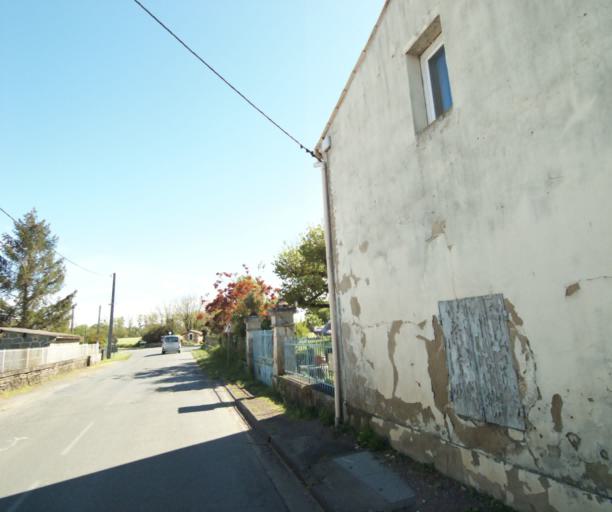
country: FR
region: Poitou-Charentes
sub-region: Departement de la Charente-Maritime
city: Bussac-sur-Charente
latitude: 45.8208
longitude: -0.6588
